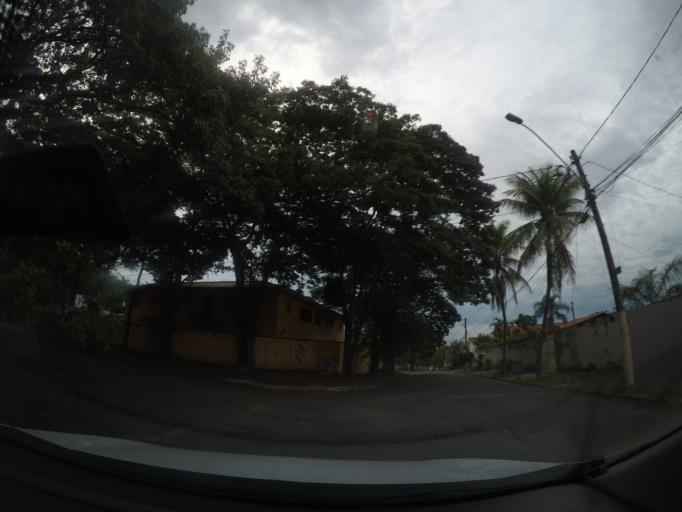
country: BR
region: Goias
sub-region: Goiania
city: Goiania
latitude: -16.6525
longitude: -49.2282
